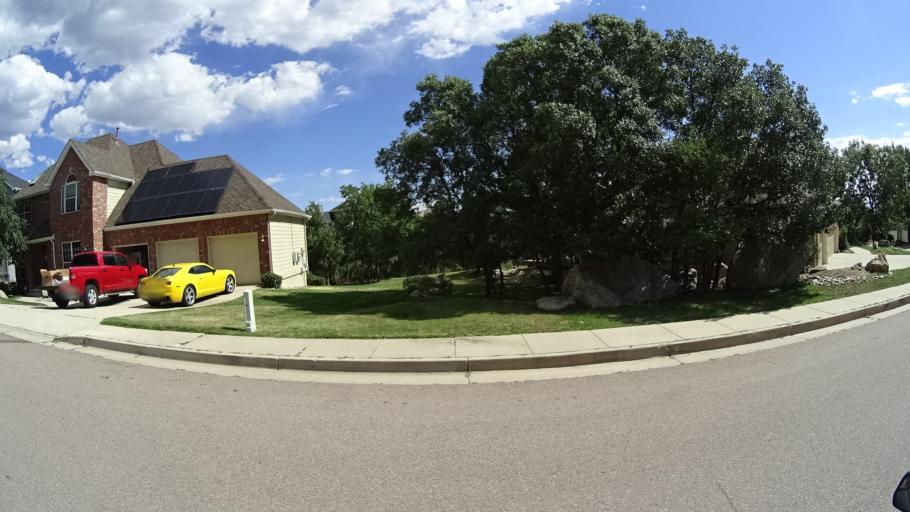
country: US
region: Colorado
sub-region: El Paso County
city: Fort Carson
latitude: 38.7499
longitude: -104.8350
